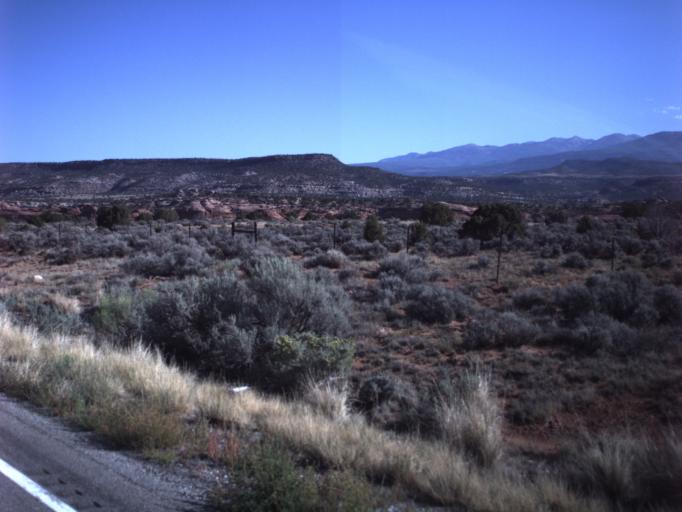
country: US
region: Utah
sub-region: Grand County
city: Moab
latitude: 38.3381
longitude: -109.4323
